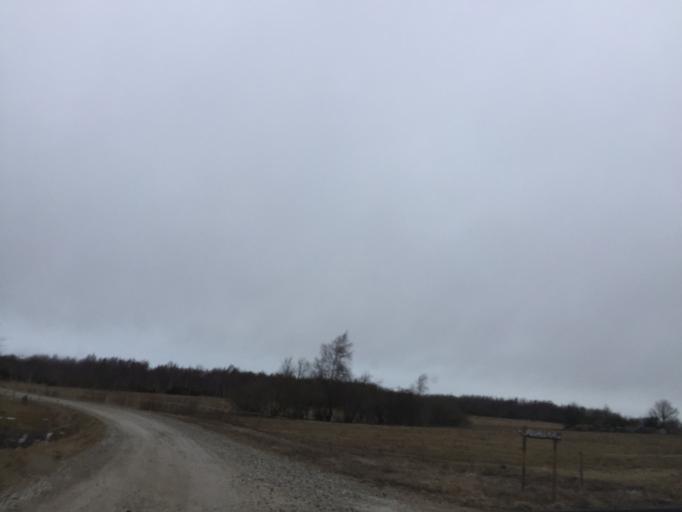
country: EE
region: Laeaene
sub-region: Haapsalu linn
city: Haapsalu
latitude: 58.6782
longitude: 23.5414
